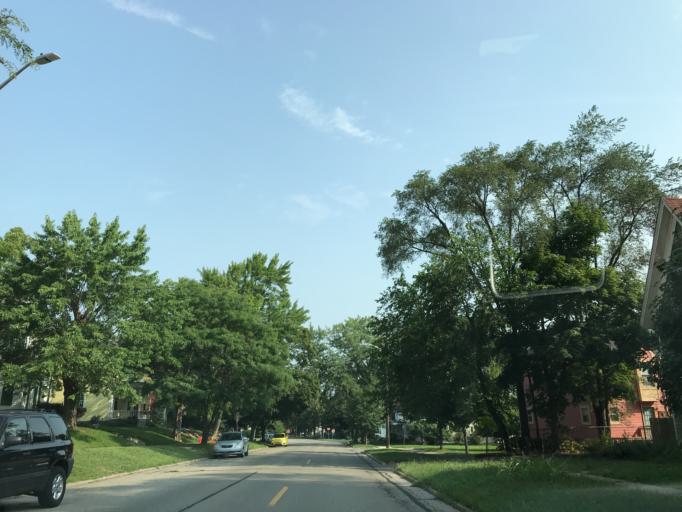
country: US
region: Michigan
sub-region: Washtenaw County
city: Ypsilanti
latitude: 42.2475
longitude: -83.6161
